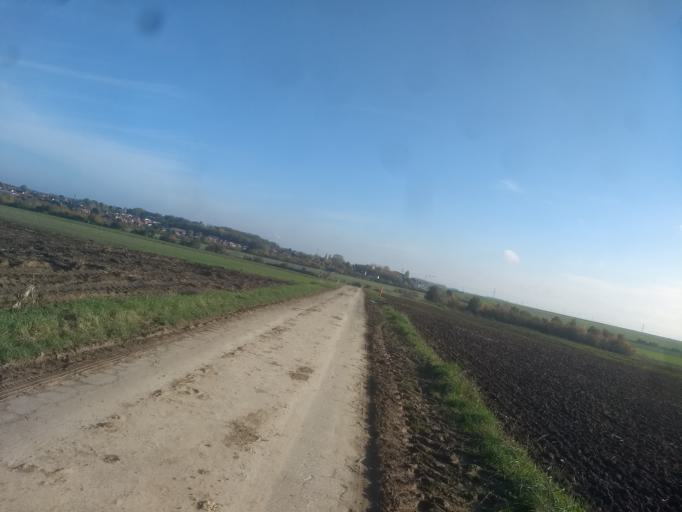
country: FR
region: Nord-Pas-de-Calais
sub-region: Departement du Pas-de-Calais
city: Beaurains
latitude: 50.2770
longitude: 2.8009
